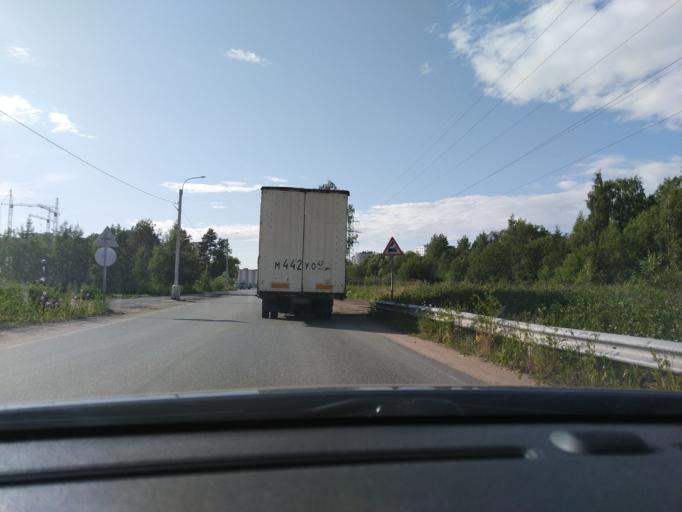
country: RU
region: St.-Petersburg
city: Gorelovo
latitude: 59.7834
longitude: 30.1703
